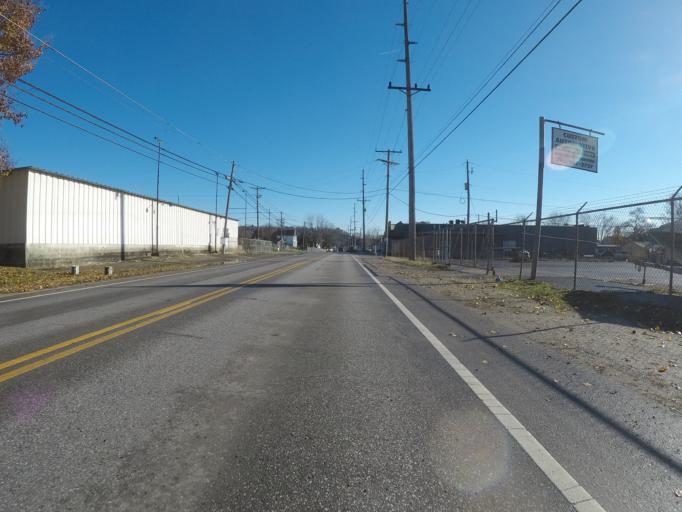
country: US
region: West Virginia
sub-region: Cabell County
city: Huntington
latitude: 38.4261
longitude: -82.4663
